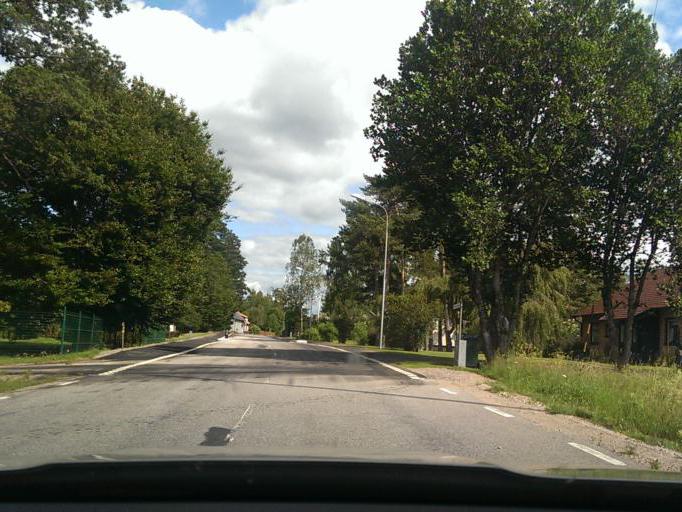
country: SE
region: Kronoberg
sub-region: Ljungby Kommun
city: Lagan
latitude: 56.9725
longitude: 13.9388
